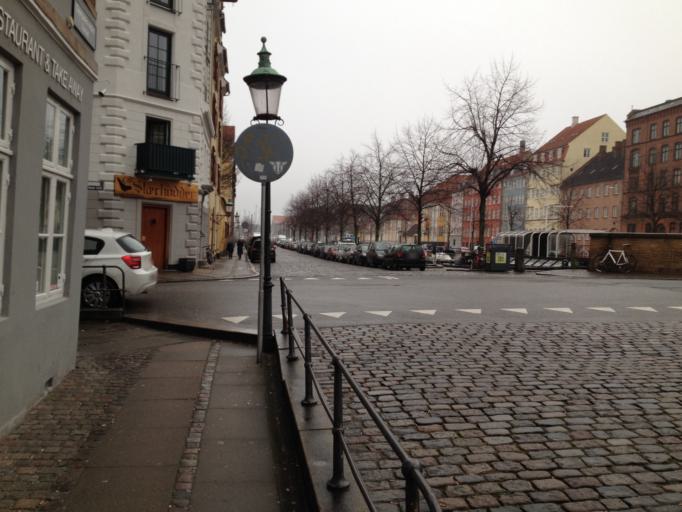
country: DK
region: Capital Region
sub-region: Kobenhavn
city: Christianshavn
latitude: 55.6734
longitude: 12.5920
